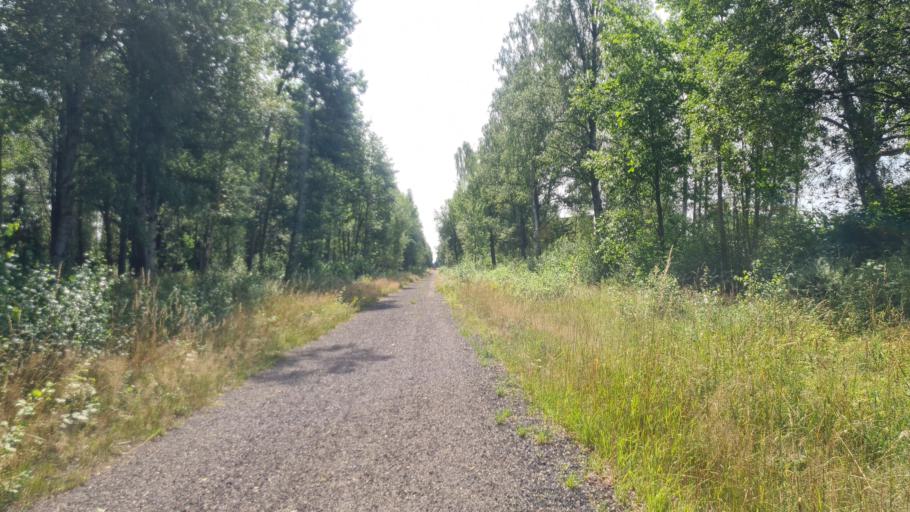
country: SE
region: Kronoberg
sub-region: Ljungby Kommun
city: Lagan
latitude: 56.9697
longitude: 13.9510
